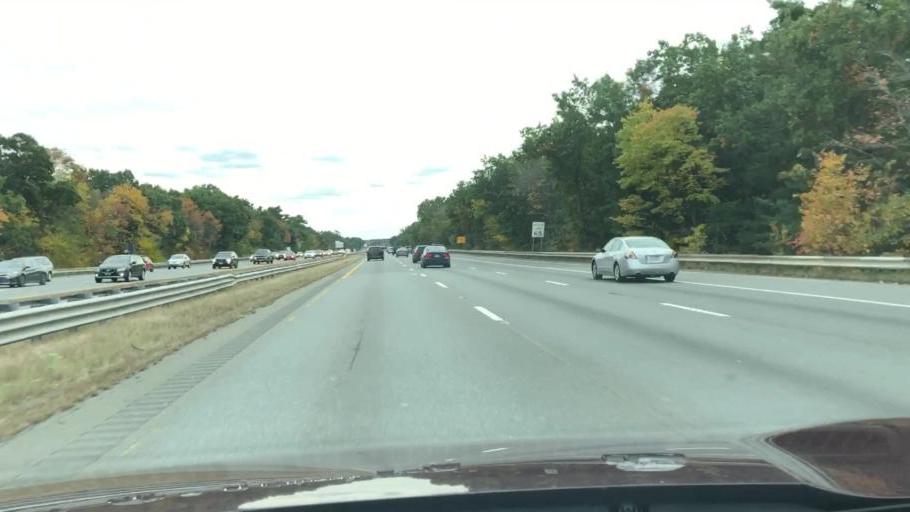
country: US
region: Massachusetts
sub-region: Essex County
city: Andover
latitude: 42.6203
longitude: -71.1767
